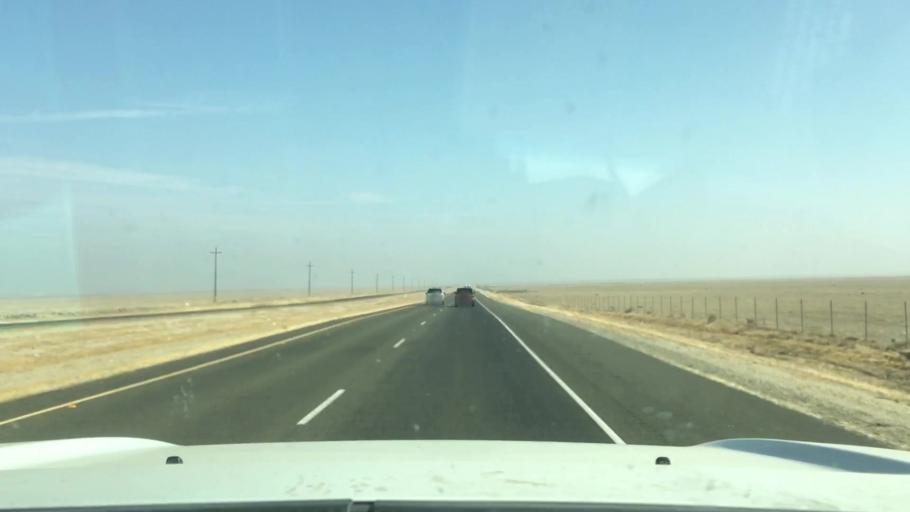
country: US
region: California
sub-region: Kern County
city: Lost Hills
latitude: 35.6155
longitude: -119.8274
